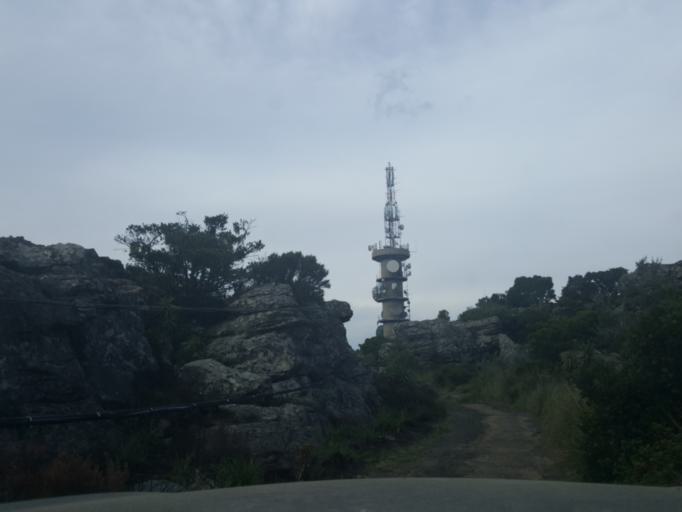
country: ZA
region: Limpopo
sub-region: Mopani District Municipality
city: Hoedspruit
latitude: -24.5410
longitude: 30.8698
